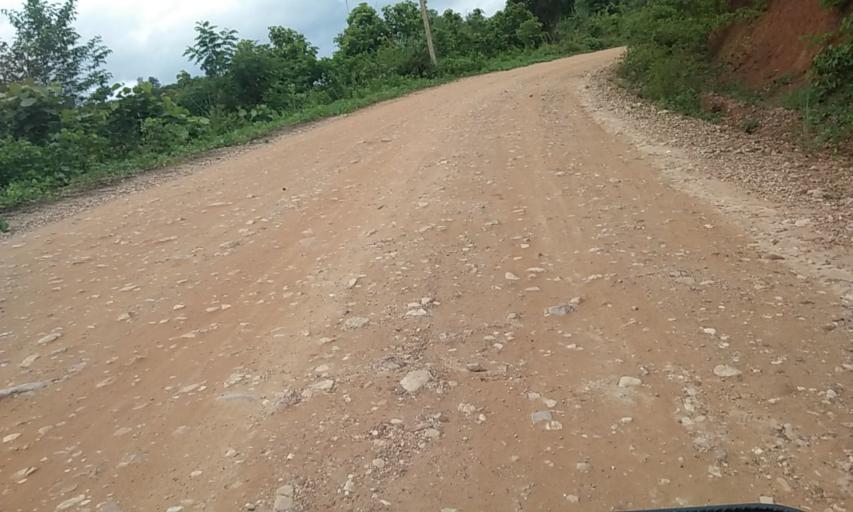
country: TH
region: Nan
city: Chaloem Phra Kiat
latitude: 19.6837
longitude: 100.8055
